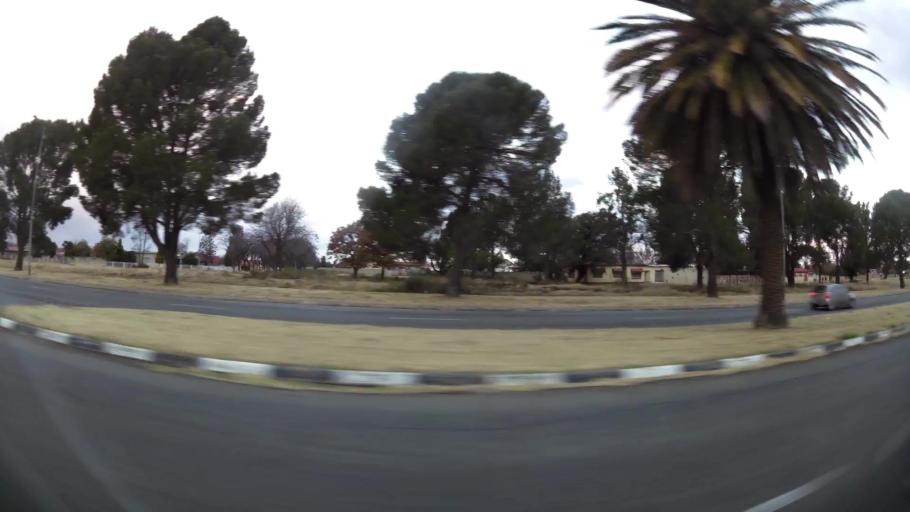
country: ZA
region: Orange Free State
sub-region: Lejweleputswa District Municipality
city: Welkom
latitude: -27.9693
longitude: 26.7645
